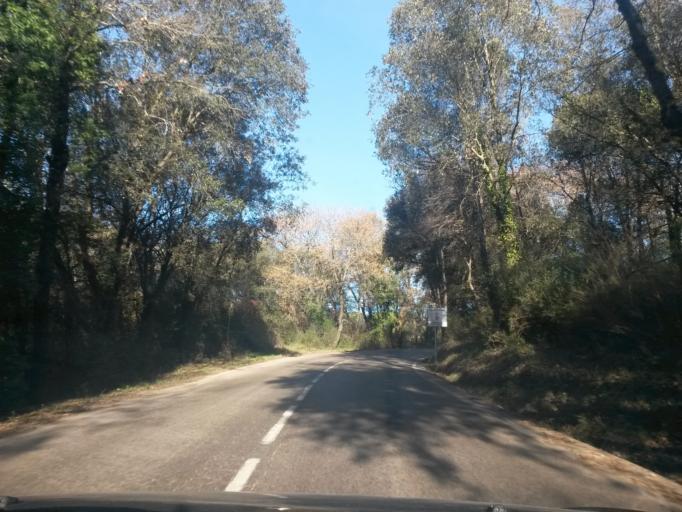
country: ES
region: Catalonia
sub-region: Provincia de Girona
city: Angles
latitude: 41.9744
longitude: 2.6708
